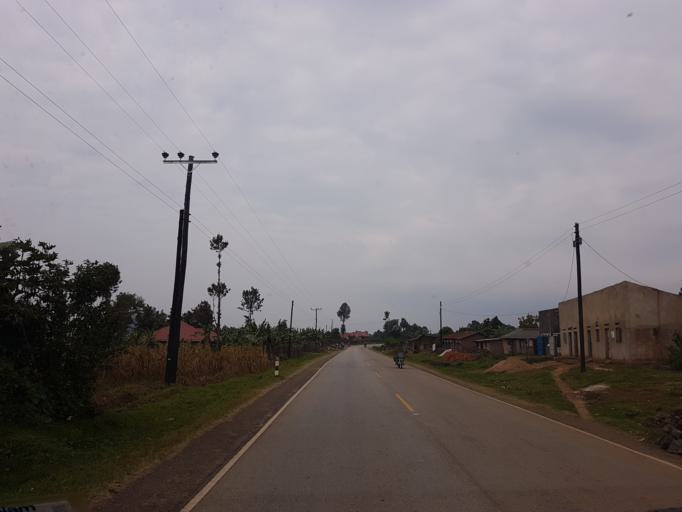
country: UG
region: Western Region
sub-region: Kisoro District
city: Kisoro
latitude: -1.3034
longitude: 29.7239
